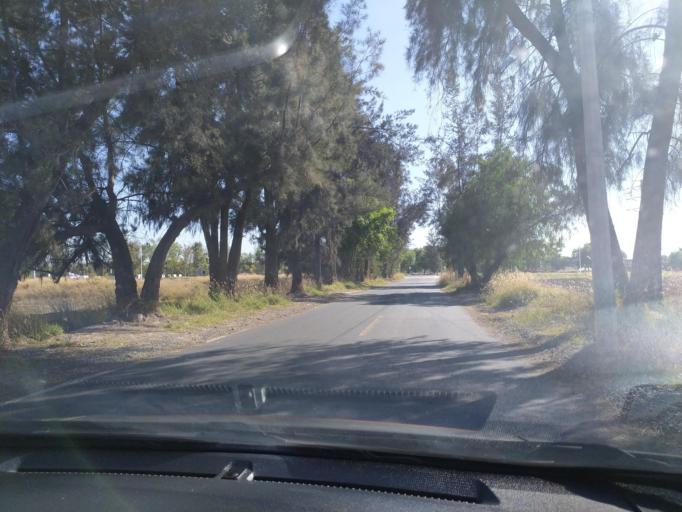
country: LA
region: Oudomxai
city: Muang La
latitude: 21.0403
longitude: 101.8378
